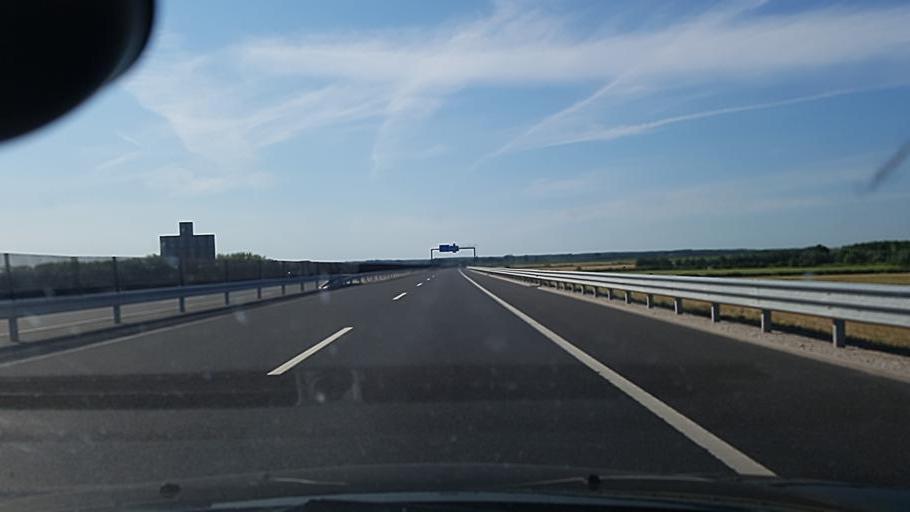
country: HU
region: Tolna
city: Tolna
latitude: 46.4023
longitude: 18.7456
